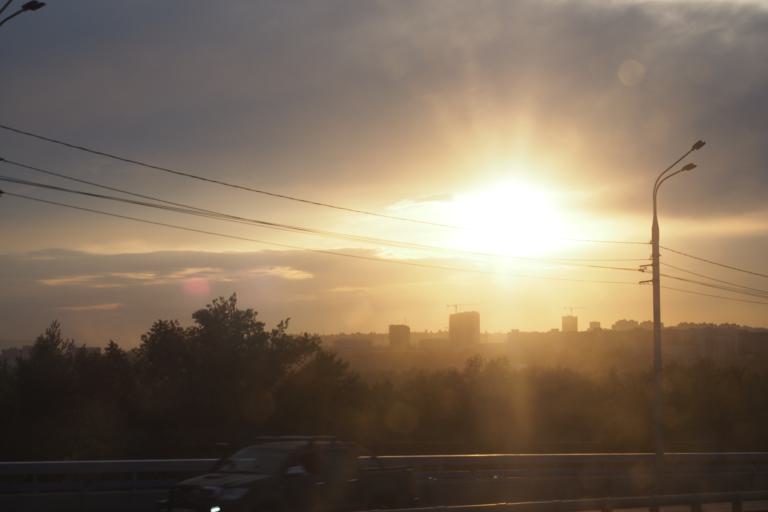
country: RU
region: Krasnoyarskiy
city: Krasnoyarsk
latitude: 56.0219
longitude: 92.9465
